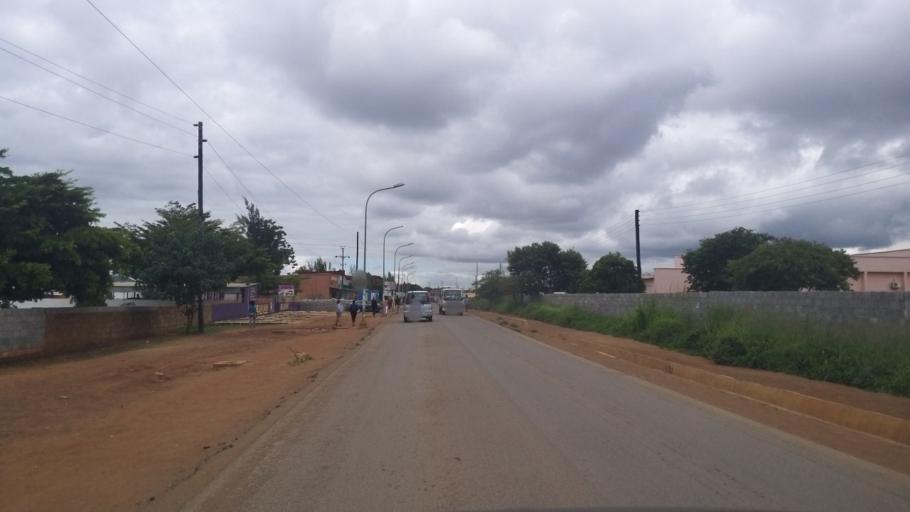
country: ZM
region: Lusaka
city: Lusaka
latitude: -15.4432
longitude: 28.3078
